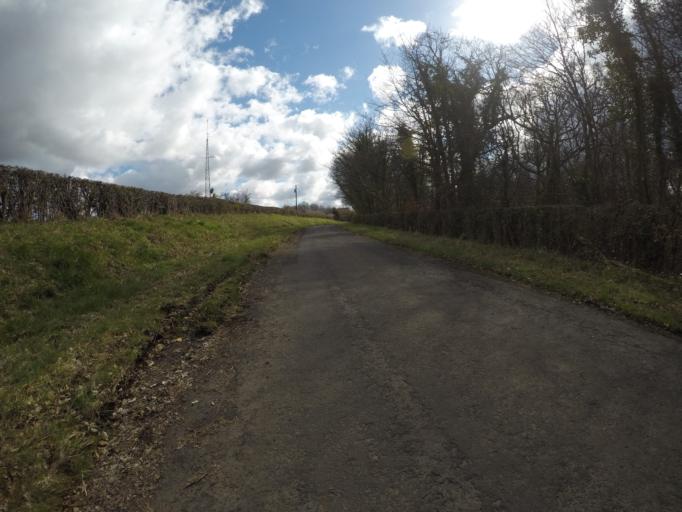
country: GB
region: Scotland
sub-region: North Ayrshire
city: Beith
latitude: 55.7370
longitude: -4.6590
